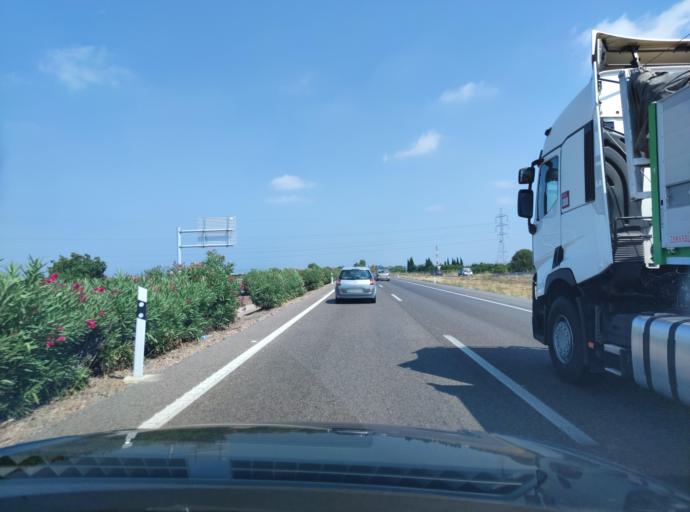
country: ES
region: Valencia
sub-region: Provincia de Castello
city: Alquerias del Nino Perdido
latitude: 39.8987
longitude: -0.1315
